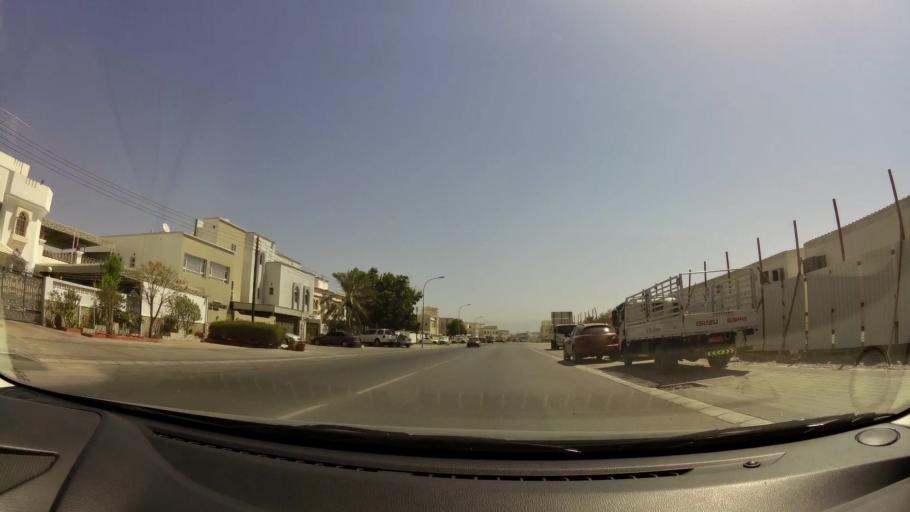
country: OM
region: Muhafazat Masqat
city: As Sib al Jadidah
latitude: 23.6223
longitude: 58.2183
